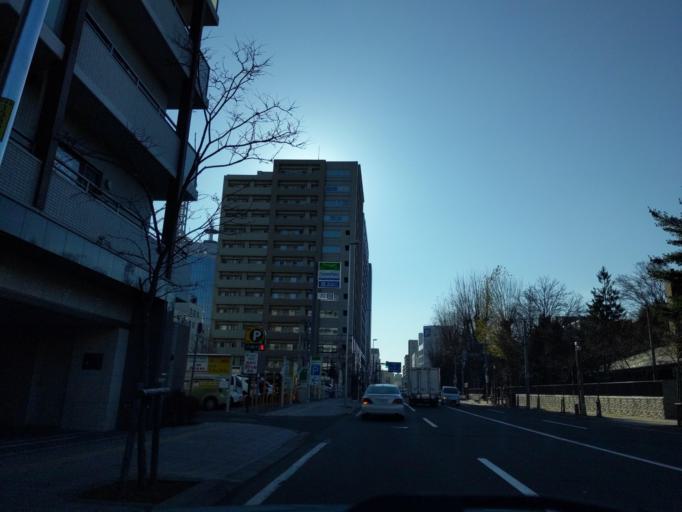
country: JP
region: Hokkaido
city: Sapporo
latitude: 43.0616
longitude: 141.3341
